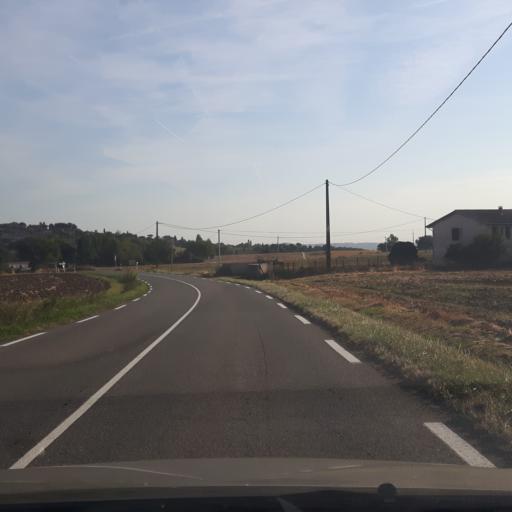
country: FR
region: Midi-Pyrenees
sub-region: Departement de la Haute-Garonne
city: Montjoire
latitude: 43.7615
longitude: 1.5250
